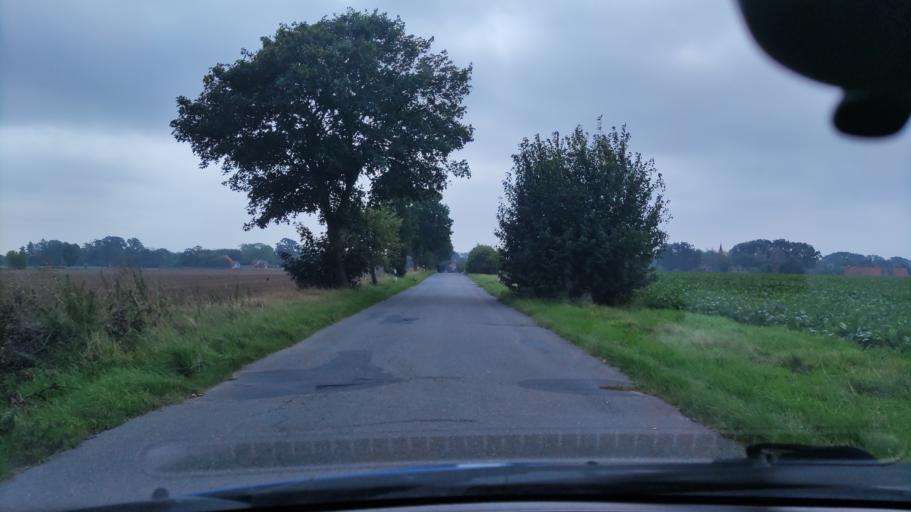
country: DE
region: Lower Saxony
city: Altenmedingen
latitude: 53.1359
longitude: 10.5991
